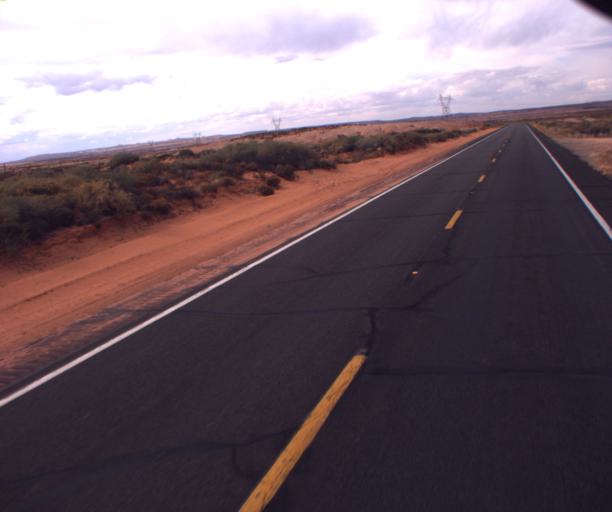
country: US
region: Arizona
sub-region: Apache County
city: Many Farms
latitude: 36.9370
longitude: -109.6359
